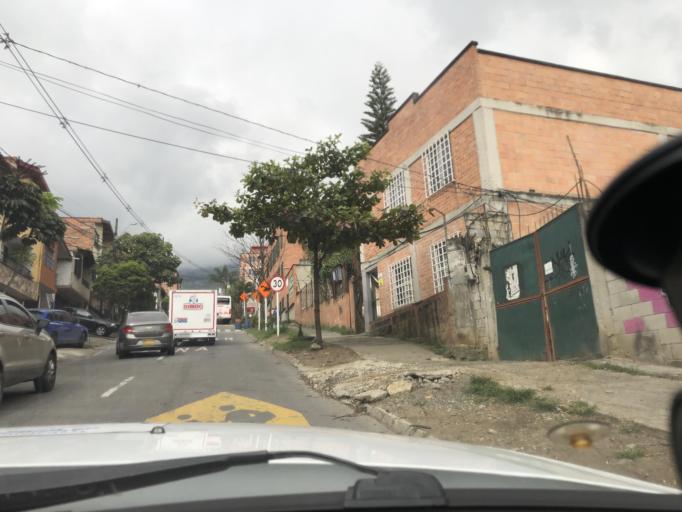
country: CO
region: Antioquia
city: Bello
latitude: 6.3136
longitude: -75.5692
